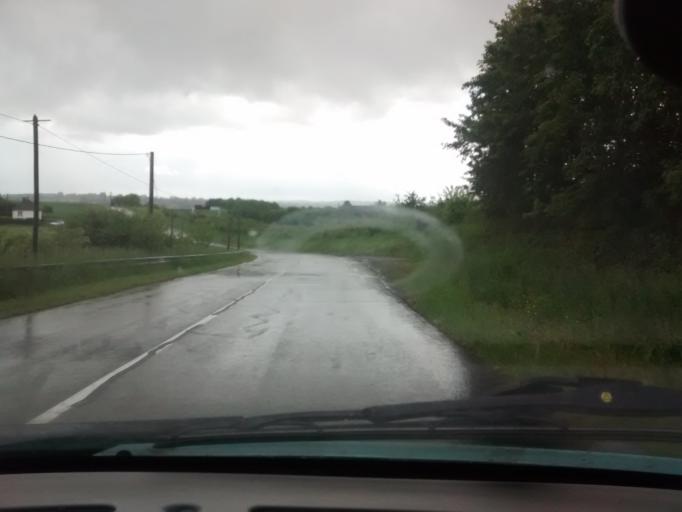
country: FR
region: Lower Normandy
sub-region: Departement de la Manche
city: Conde-sur-Vire
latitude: 49.0679
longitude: -1.0192
